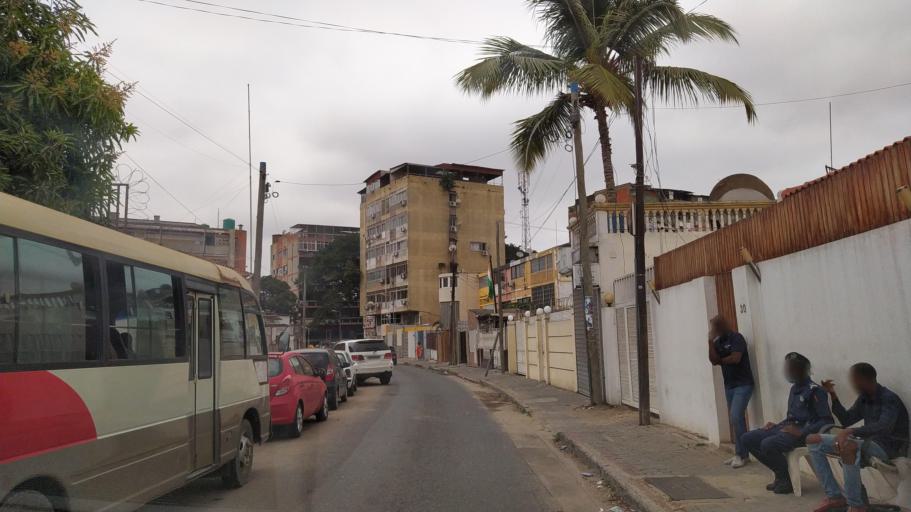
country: AO
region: Luanda
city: Luanda
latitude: -8.8290
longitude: 13.2533
